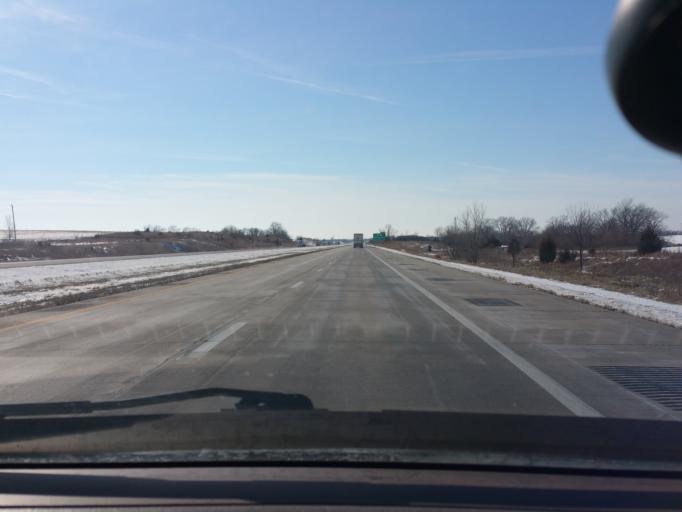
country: US
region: Missouri
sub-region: Harrison County
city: Bethany
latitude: 40.1726
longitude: -94.0203
